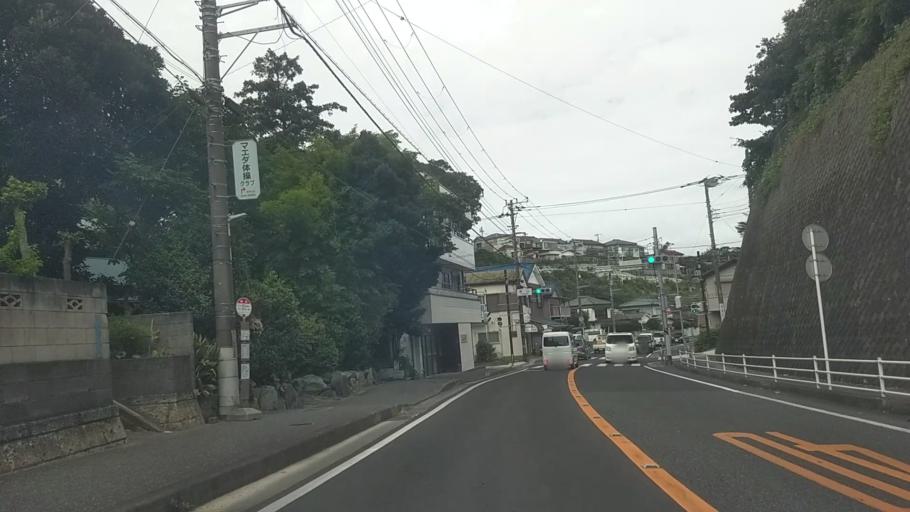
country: JP
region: Kanagawa
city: Yokosuka
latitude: 35.2461
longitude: 139.7250
